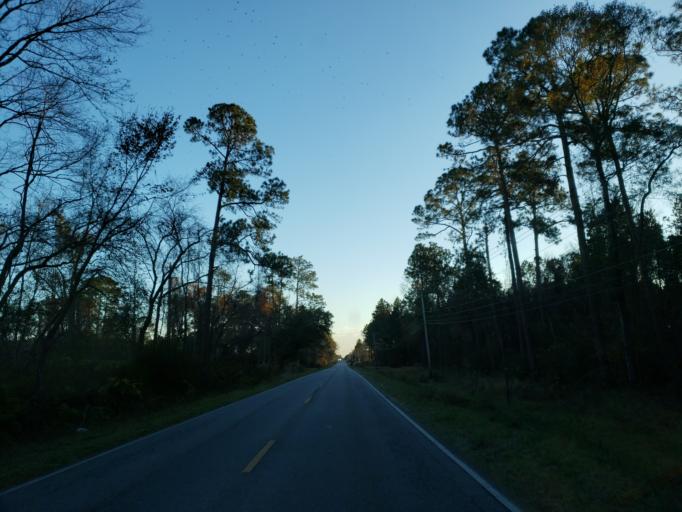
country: US
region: Georgia
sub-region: Crisp County
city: Cordele
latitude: 31.9480
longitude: -83.7657
